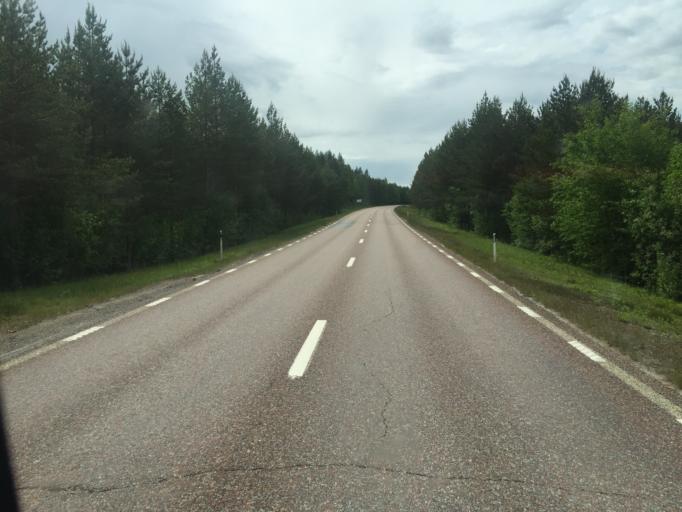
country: SE
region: Dalarna
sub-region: Vansbro Kommun
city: Vansbro
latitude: 60.4788
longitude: 14.1102
